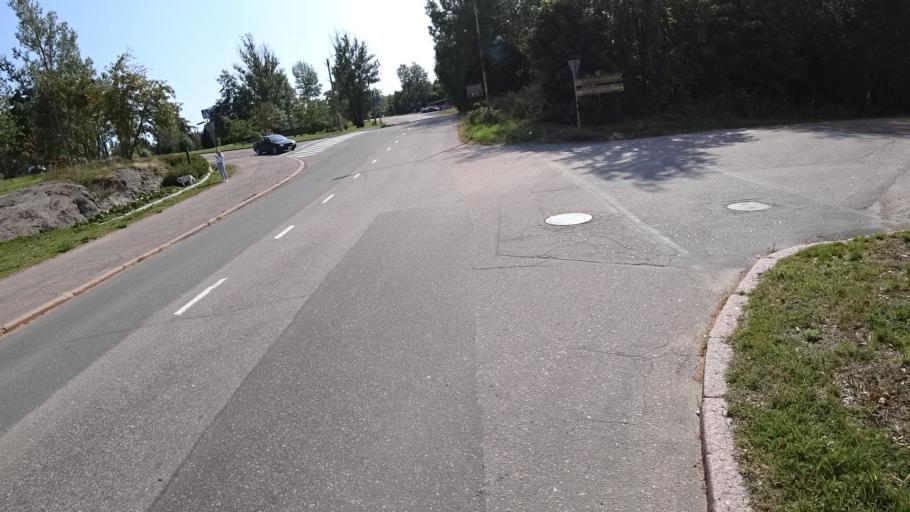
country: FI
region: Kymenlaakso
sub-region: Kotka-Hamina
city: Kotka
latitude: 60.4554
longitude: 26.9367
